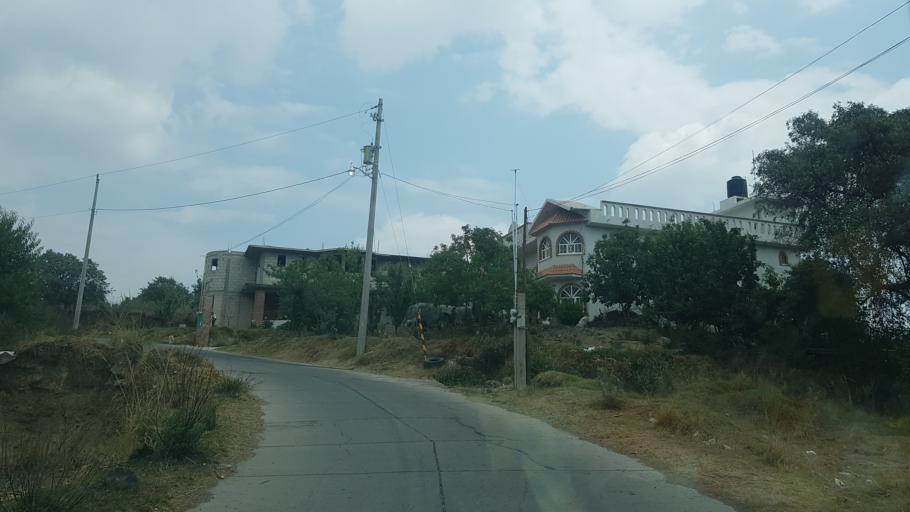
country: MX
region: Puebla
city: Domingo Arenas
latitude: 19.1394
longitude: -98.4766
